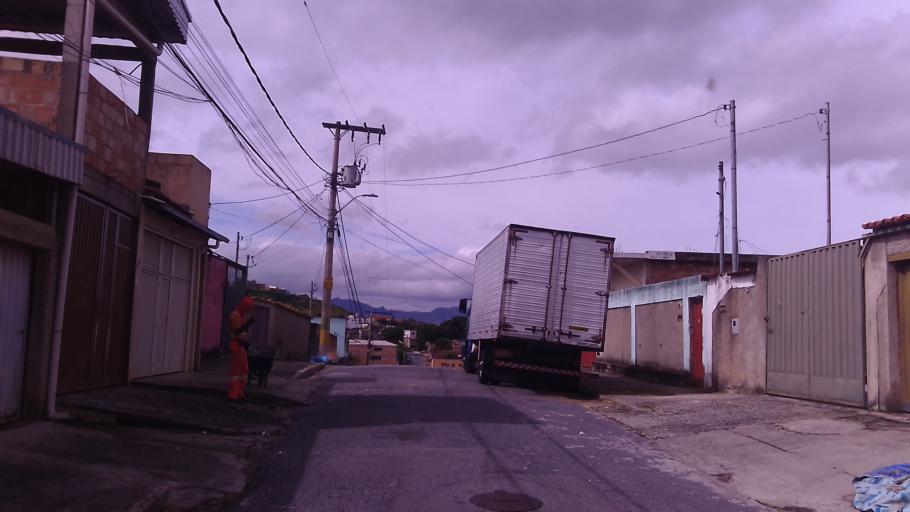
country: BR
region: Minas Gerais
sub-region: Santa Luzia
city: Santa Luzia
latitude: -19.8375
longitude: -43.8938
